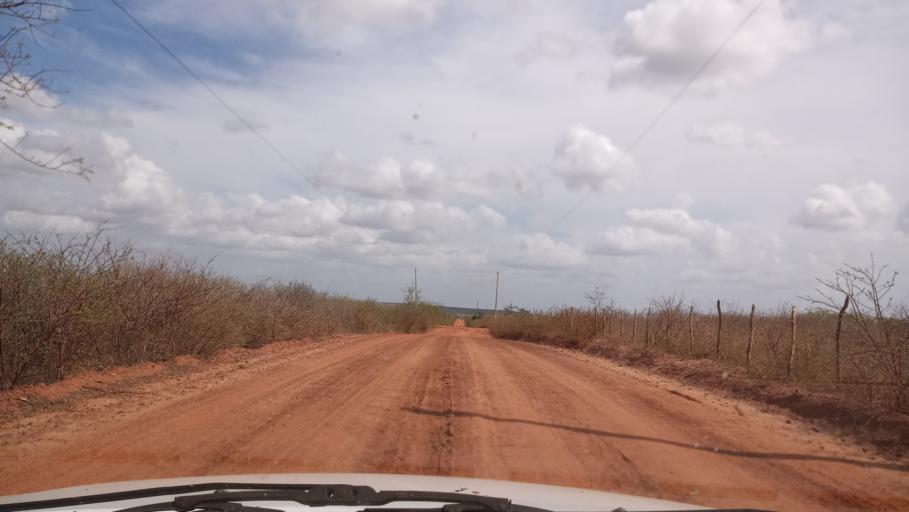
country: BR
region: Rio Grande do Norte
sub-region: Joao Camara
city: Joao Camara
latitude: -5.4553
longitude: -35.8390
